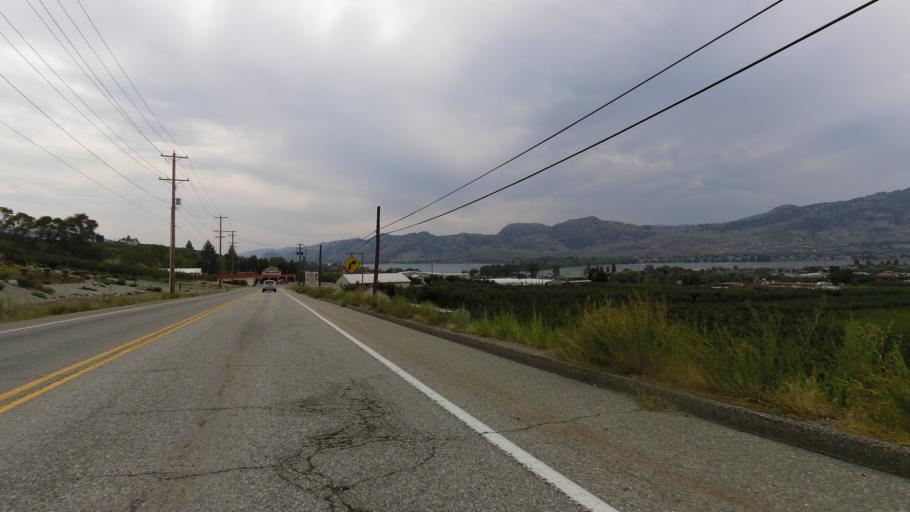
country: CA
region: British Columbia
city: Osoyoos
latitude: 49.0298
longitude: -119.4314
